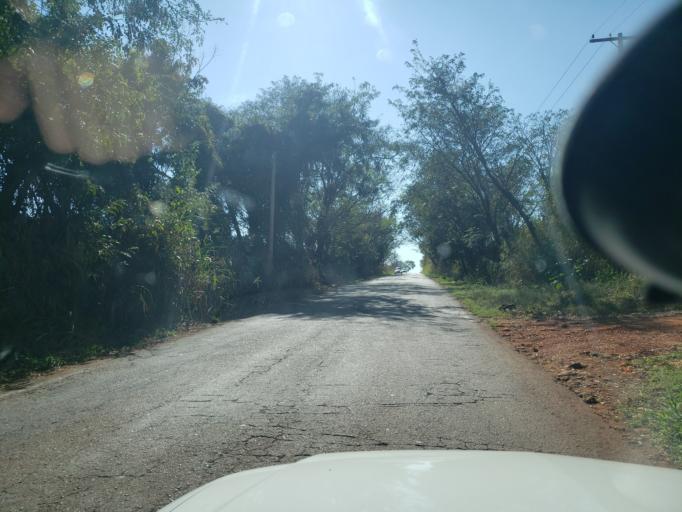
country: BR
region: Sao Paulo
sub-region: Moji-Guacu
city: Mogi-Gaucu
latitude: -22.3426
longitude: -46.8896
